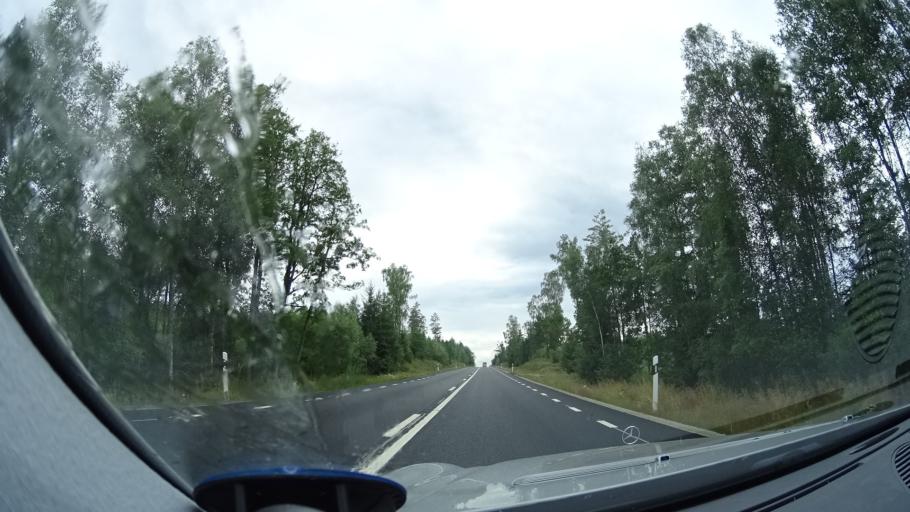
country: SE
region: Kronoberg
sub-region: Tingsryds Kommun
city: Tingsryd
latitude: 56.4026
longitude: 14.9275
